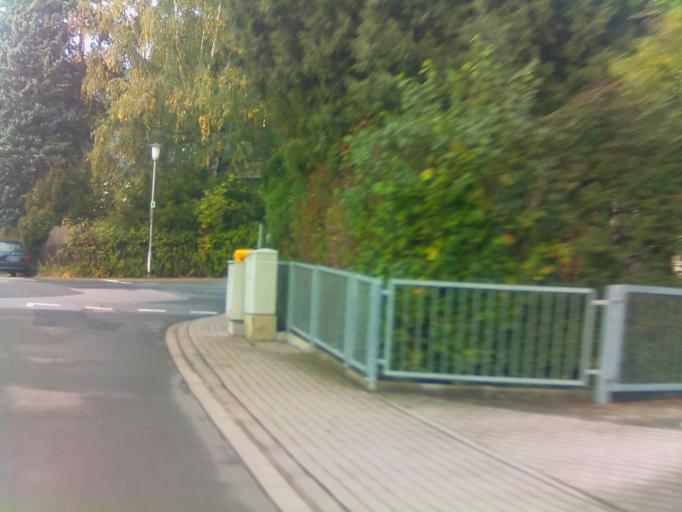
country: DE
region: Hesse
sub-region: Regierungsbezirk Darmstadt
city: Morlenbach
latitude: 49.5918
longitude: 8.7331
